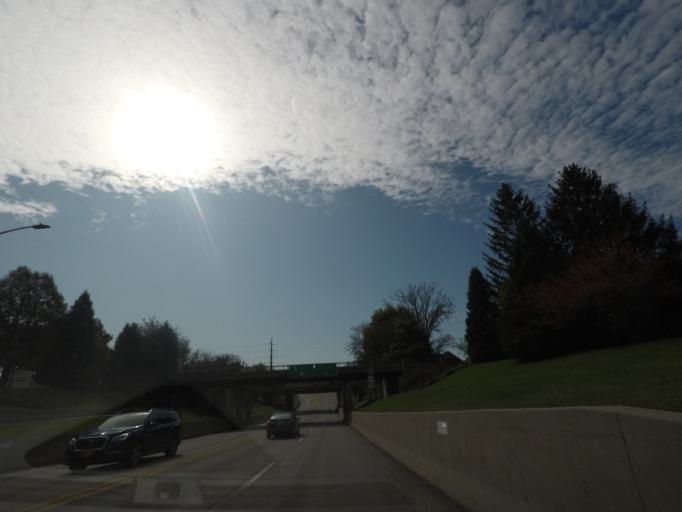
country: US
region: Iowa
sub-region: Story County
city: Ames
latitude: 42.0254
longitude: -93.6203
